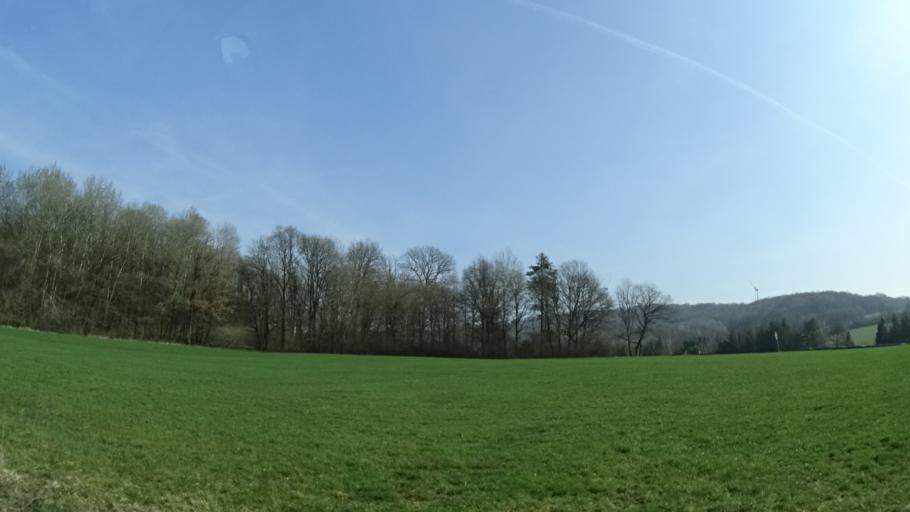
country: DE
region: Rheinland-Pfalz
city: Gimbweiler
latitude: 49.5749
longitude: 7.1826
